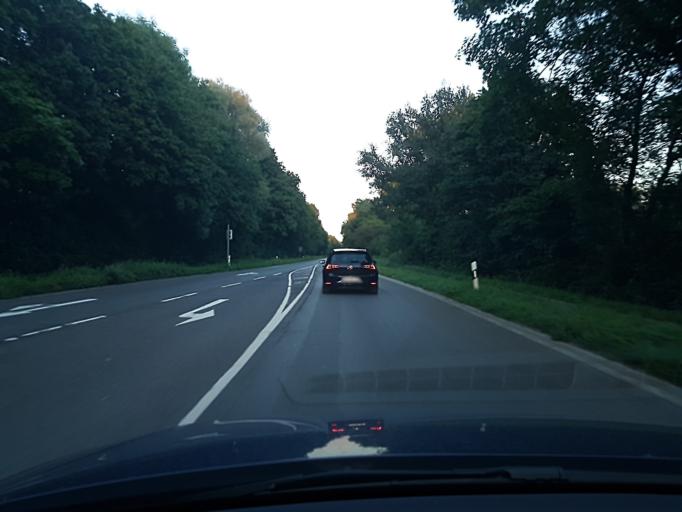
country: DE
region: North Rhine-Westphalia
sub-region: Regierungsbezirk Dusseldorf
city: Erkrath
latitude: 51.1984
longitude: 6.8956
